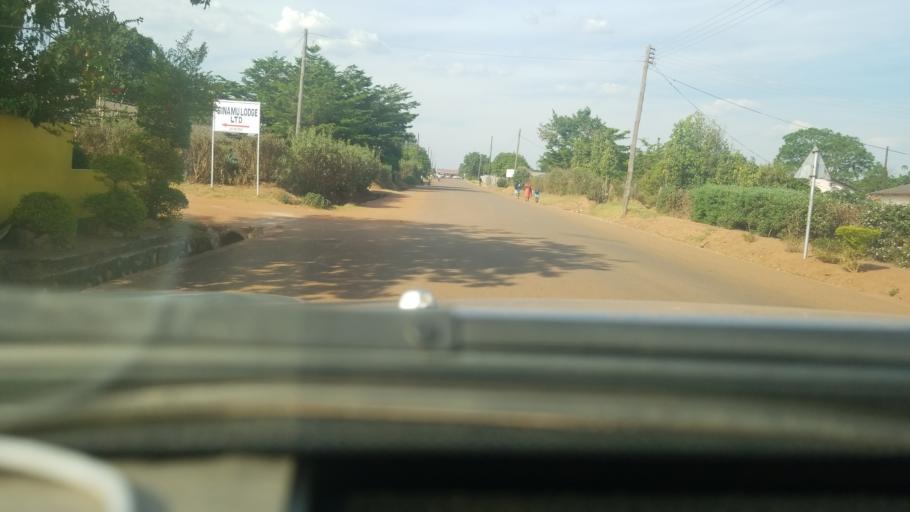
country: ZM
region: Northern
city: Kasama
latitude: -10.2048
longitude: 31.1842
